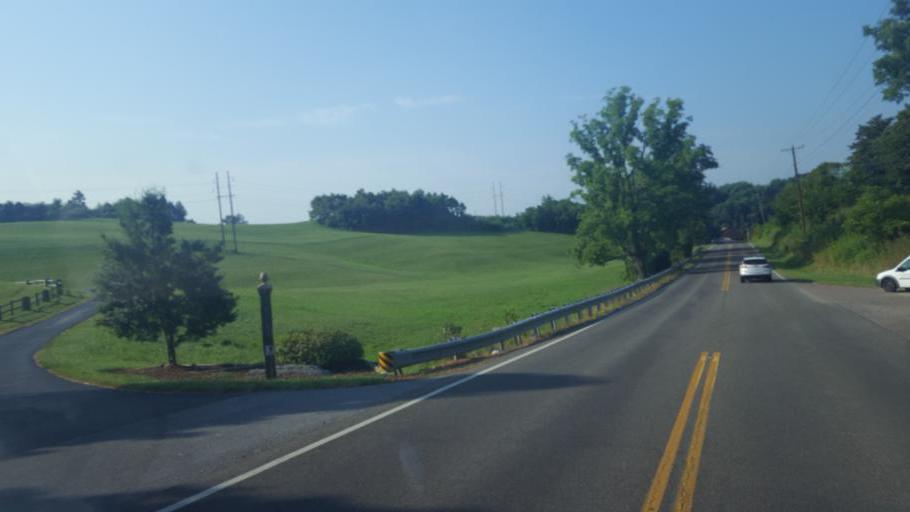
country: US
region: Tennessee
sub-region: Sullivan County
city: Bluff City
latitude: 36.4898
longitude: -82.2630
